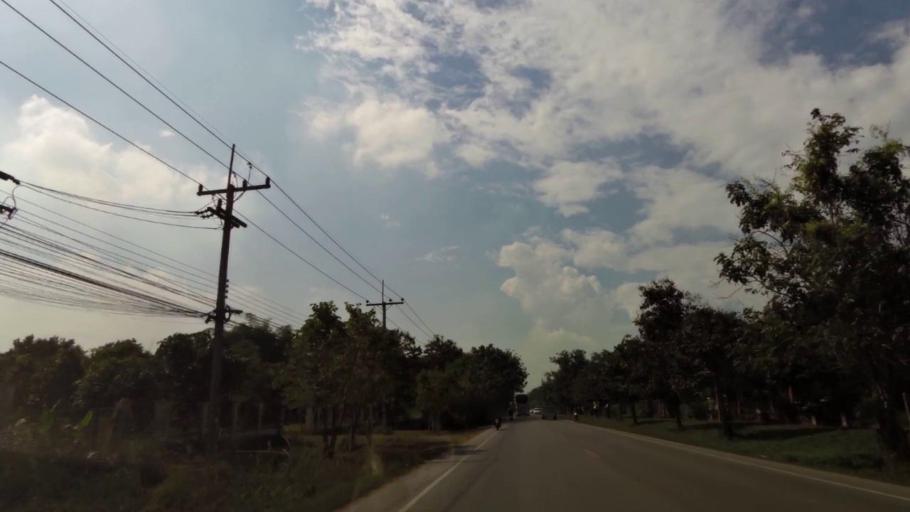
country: TH
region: Chiang Rai
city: Mae Lao
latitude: 19.8566
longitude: 99.7577
